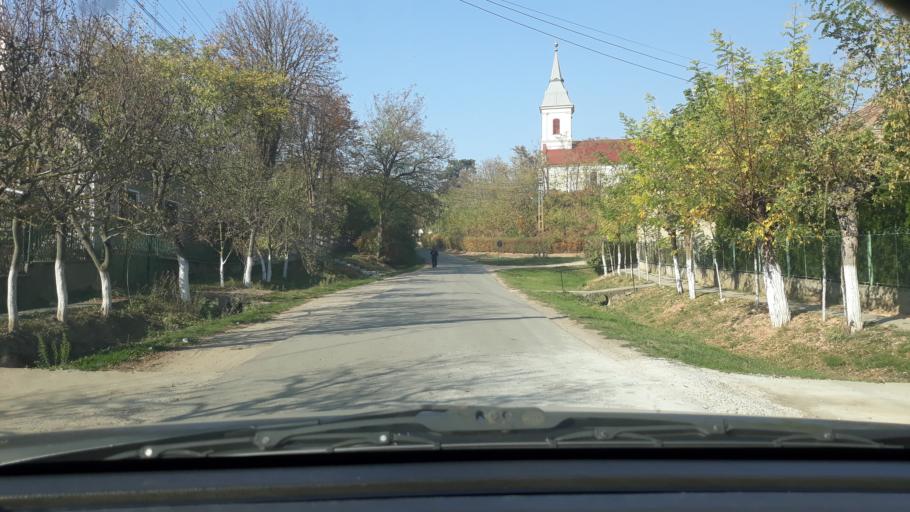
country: RO
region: Bihor
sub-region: Comuna Tarcea
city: Galospetreu
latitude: 47.4813
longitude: 22.2173
